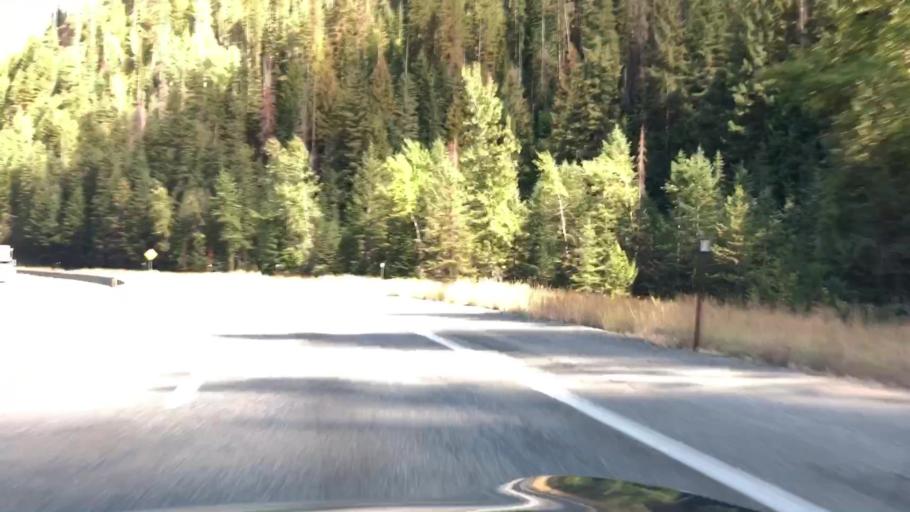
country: US
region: Idaho
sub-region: Shoshone County
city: Wallace
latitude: 47.4721
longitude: -115.8833
